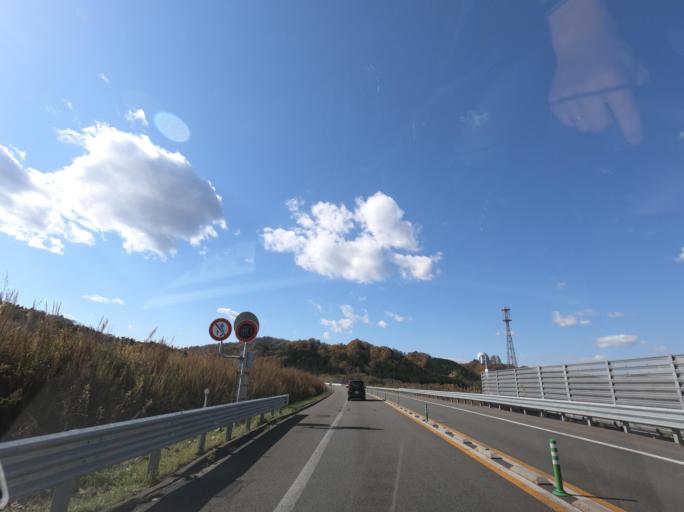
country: JP
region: Hokkaido
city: Kushiro
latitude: 43.0886
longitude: 143.9233
